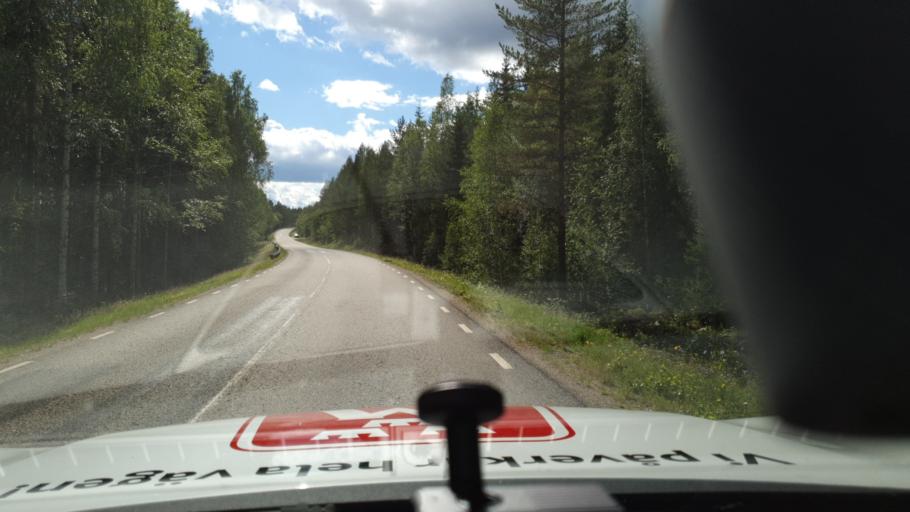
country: NO
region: Hedmark
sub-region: Trysil
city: Innbygda
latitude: 61.0290
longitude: 12.5669
